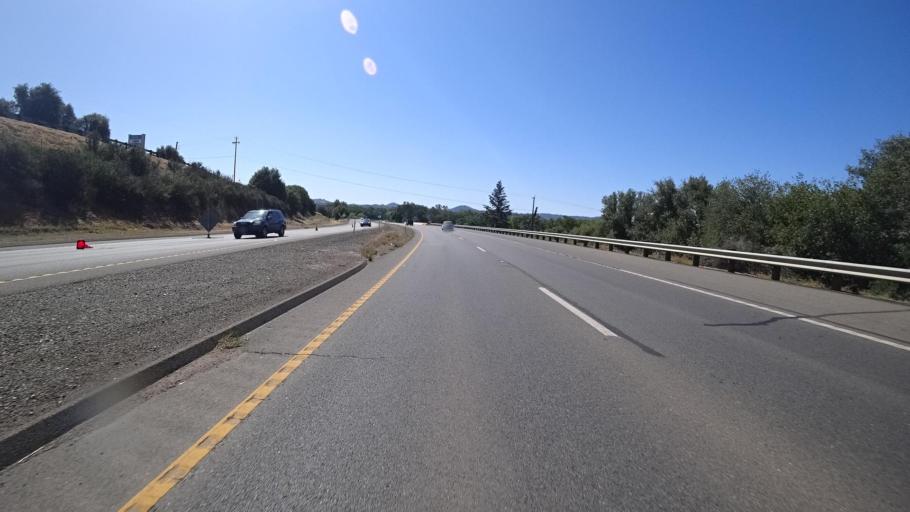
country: US
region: California
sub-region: Lake County
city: Lower Lake
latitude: 38.9285
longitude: -122.6183
